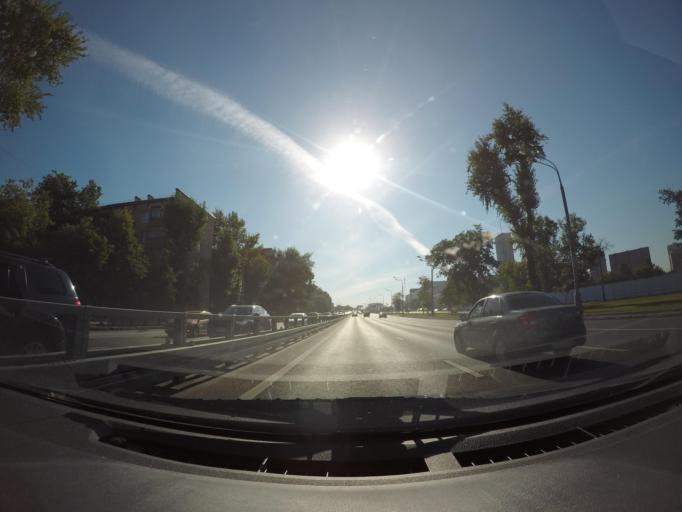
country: RU
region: Moscow
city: Ryazanskiy
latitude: 55.7305
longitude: 37.7423
